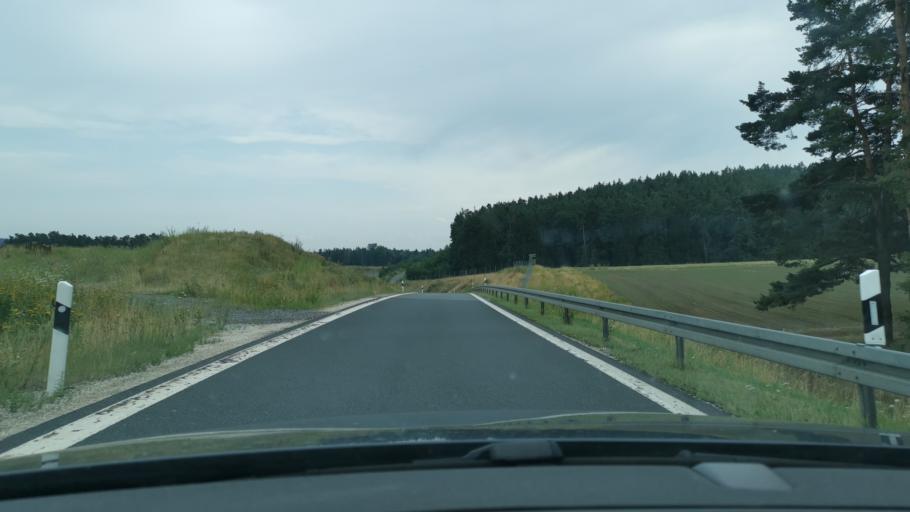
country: DE
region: Bavaria
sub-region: Upper Palatinate
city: Wernberg-Koblitz
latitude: 49.5200
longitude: 12.1609
